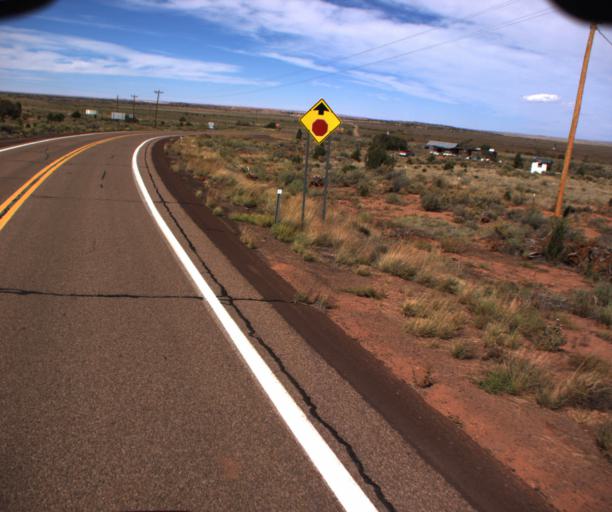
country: US
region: Arizona
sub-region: Apache County
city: Saint Johns
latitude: 34.6176
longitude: -109.6620
